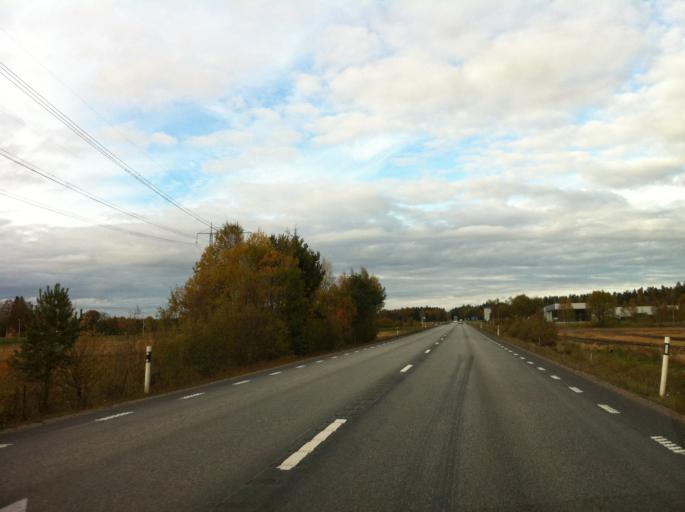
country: SE
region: OErebro
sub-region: Askersunds Kommun
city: Asbro
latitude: 58.9692
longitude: 15.0368
